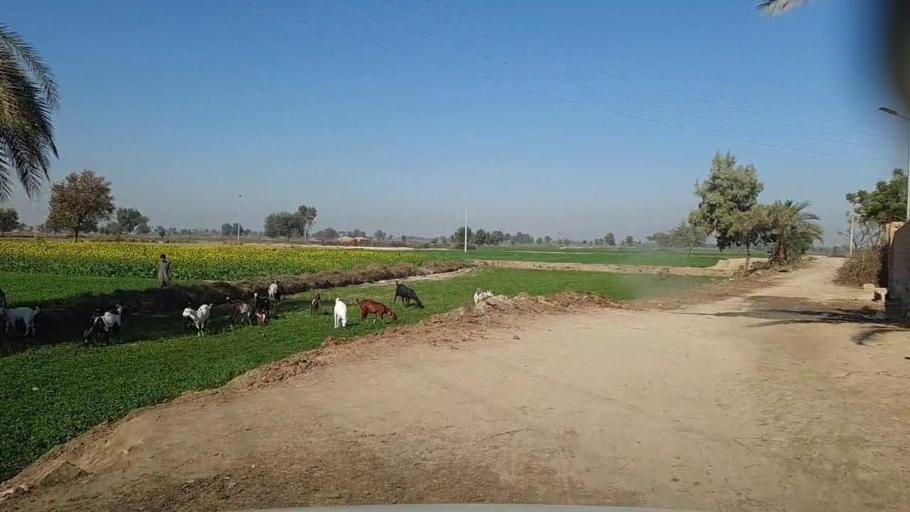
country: PK
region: Sindh
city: Khairpur
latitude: 28.0603
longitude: 69.7392
